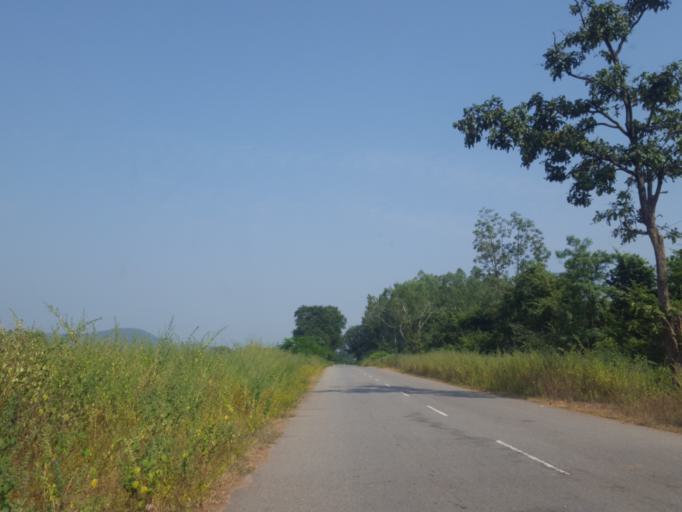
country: IN
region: Telangana
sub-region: Khammam
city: Yellandu
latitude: 17.6664
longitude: 80.2743
